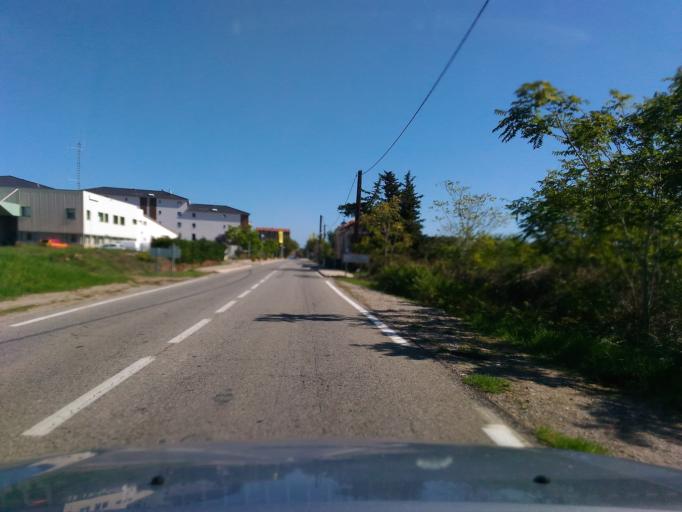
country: FR
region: Corsica
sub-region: Departement de la Haute-Corse
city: Aleria
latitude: 42.1127
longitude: 9.5100
